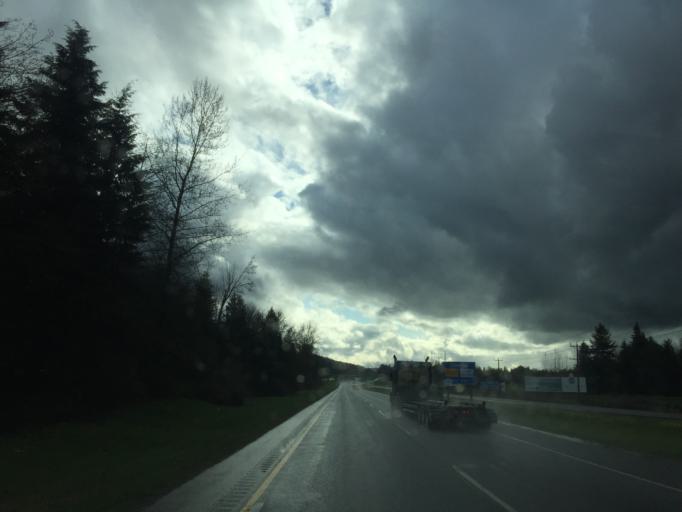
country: CA
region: British Columbia
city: Agassiz
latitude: 49.2035
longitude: -121.7203
